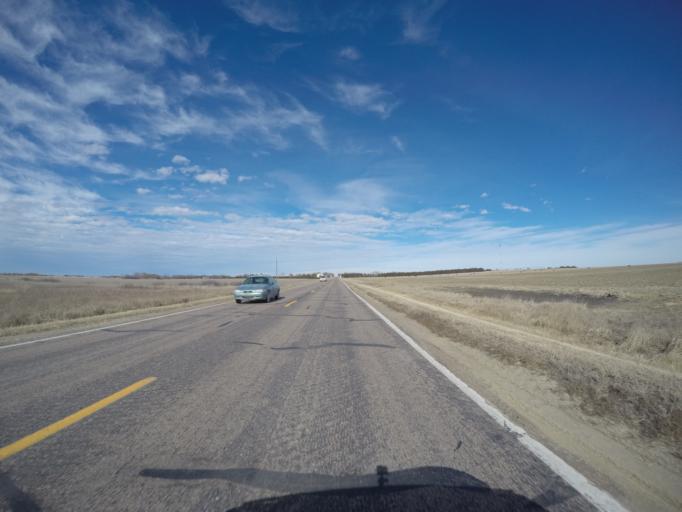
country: US
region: Nebraska
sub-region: Franklin County
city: Franklin
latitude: 40.1969
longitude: -98.9525
